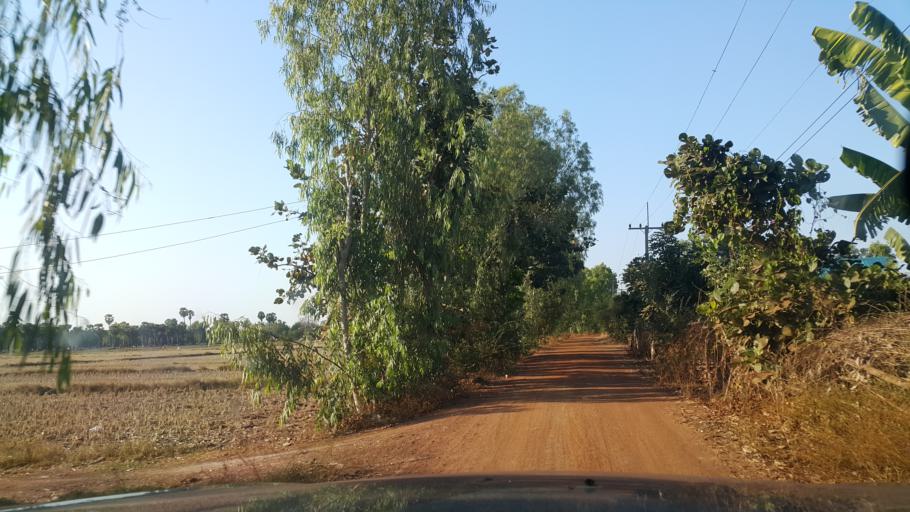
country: TH
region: Changwat Udon Thani
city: Ban Na Muang
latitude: 17.2269
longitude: 103.0447
